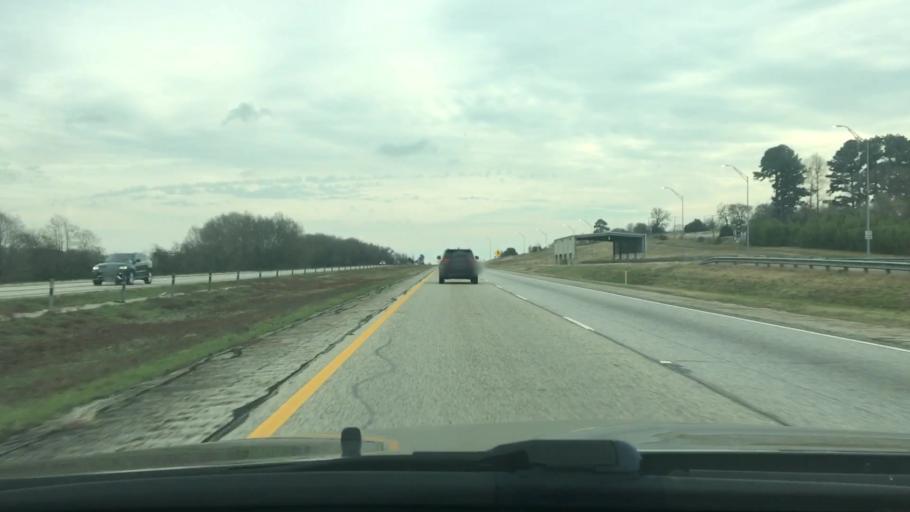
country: US
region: Texas
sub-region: Leon County
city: Centerville
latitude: 31.2801
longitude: -95.9910
